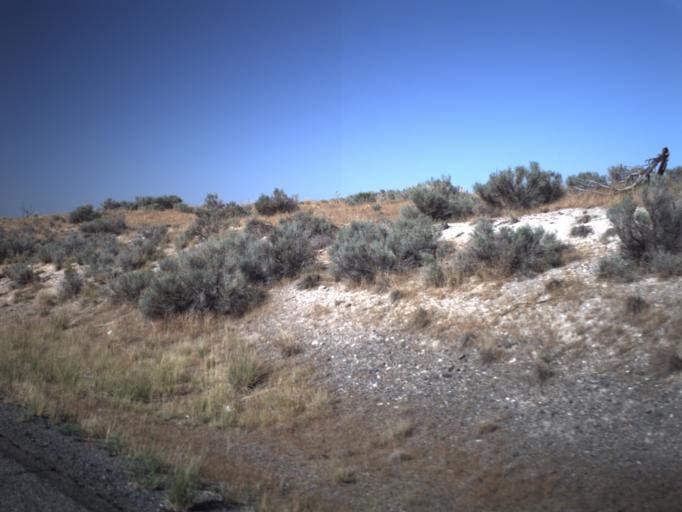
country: US
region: Utah
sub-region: Juab County
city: Mona
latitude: 39.7515
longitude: -112.1832
